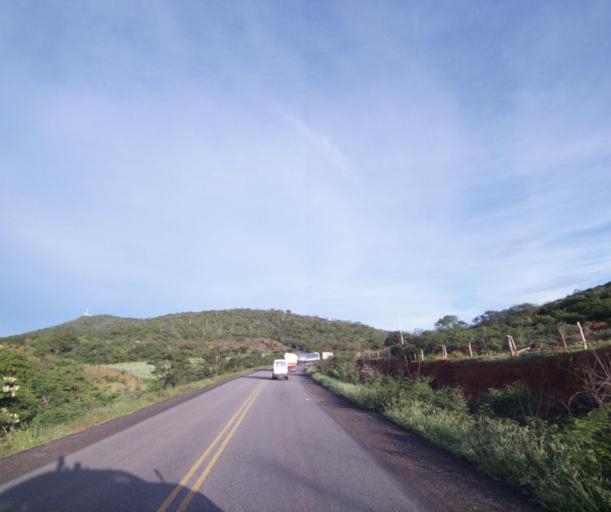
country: BR
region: Bahia
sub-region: Cacule
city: Cacule
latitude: -14.1933
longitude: -42.1448
